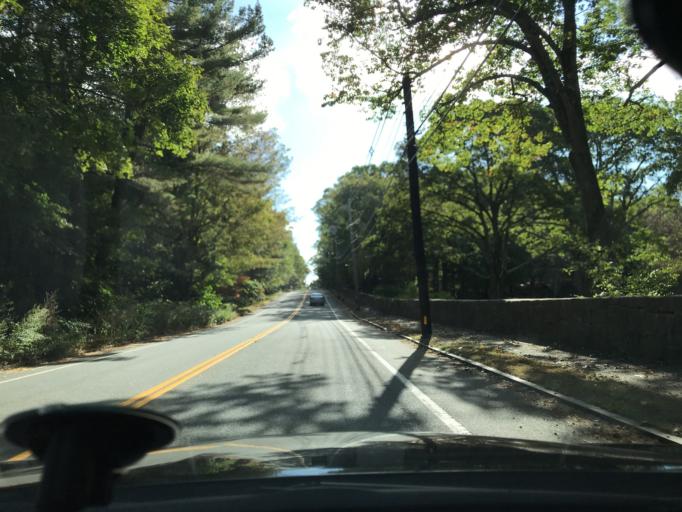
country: US
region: Massachusetts
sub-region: Suffolk County
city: Jamaica Plain
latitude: 42.3046
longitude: -71.1453
